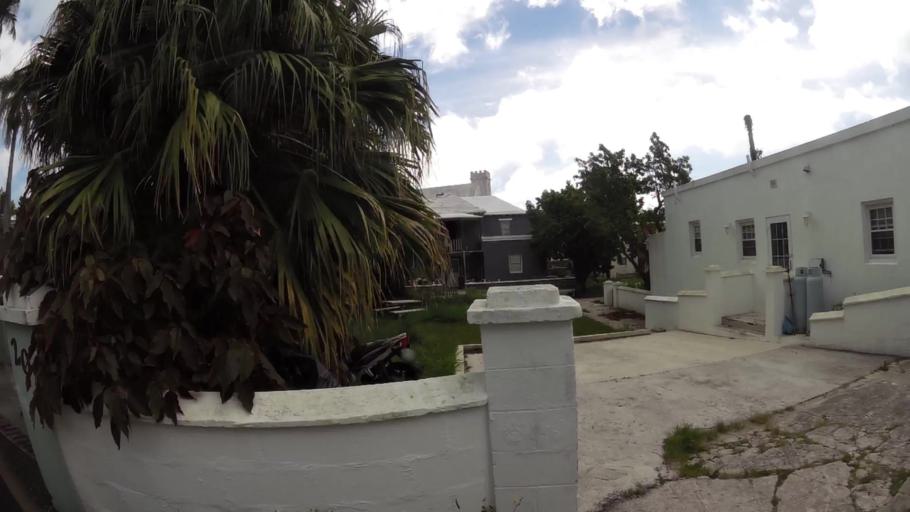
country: BM
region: Saint George
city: Saint George
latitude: 32.3828
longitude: -64.6782
